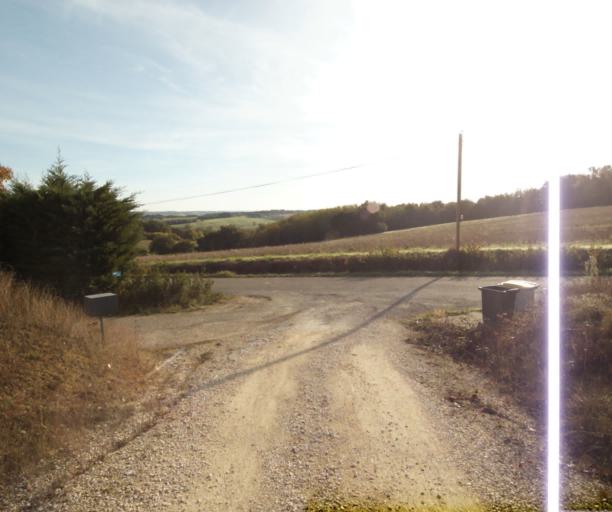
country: FR
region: Midi-Pyrenees
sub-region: Departement de la Haute-Garonne
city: Villemur-sur-Tarn
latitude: 43.9095
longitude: 1.4918
